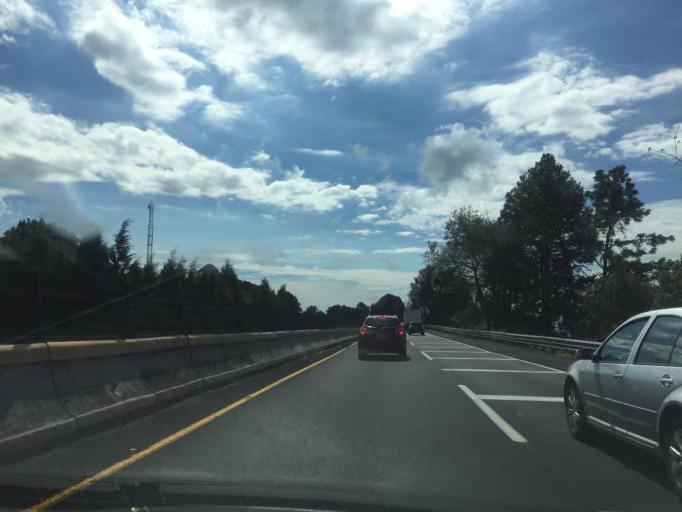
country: MX
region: Morelos
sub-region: Cuernavaca
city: Villa Santiago
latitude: 19.0265
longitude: -99.1975
